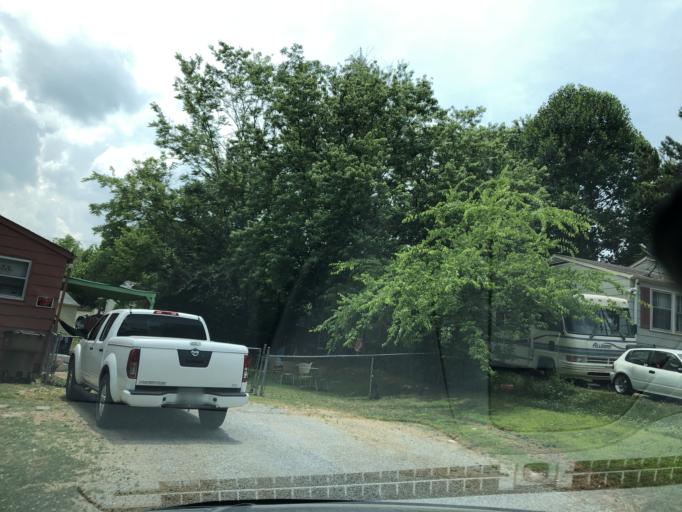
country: US
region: Tennessee
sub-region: Davidson County
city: Oak Hill
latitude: 36.0630
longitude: -86.6926
